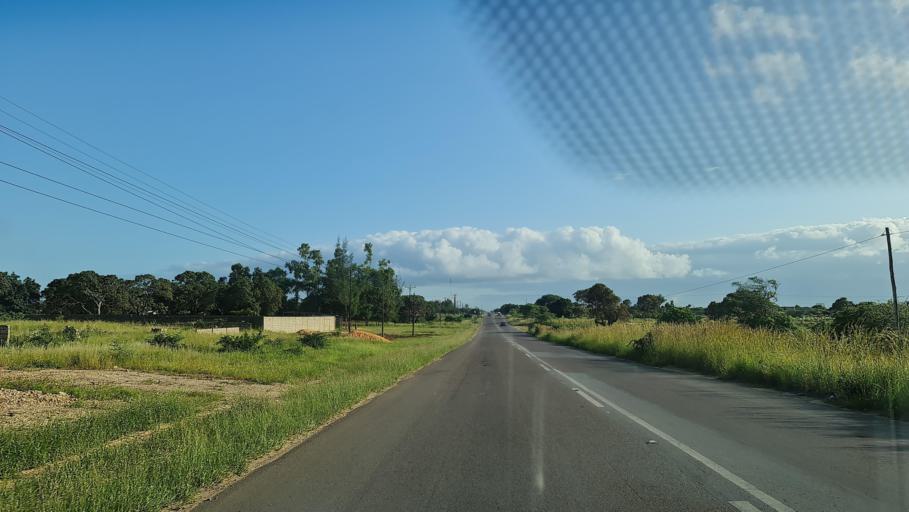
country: MZ
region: Maputo City
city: Maputo
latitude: -25.6790
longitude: 32.6668
